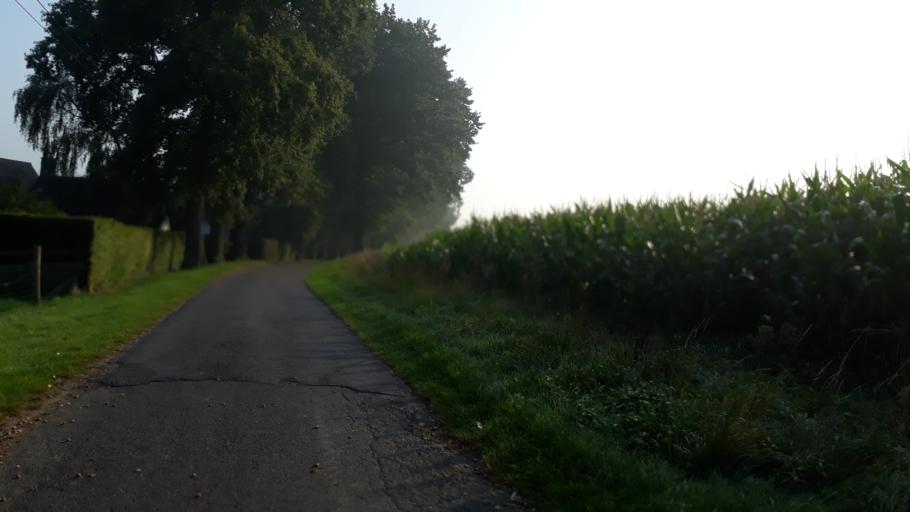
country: BE
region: Flanders
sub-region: Provincie West-Vlaanderen
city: Torhout
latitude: 51.0901
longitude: 3.0754
